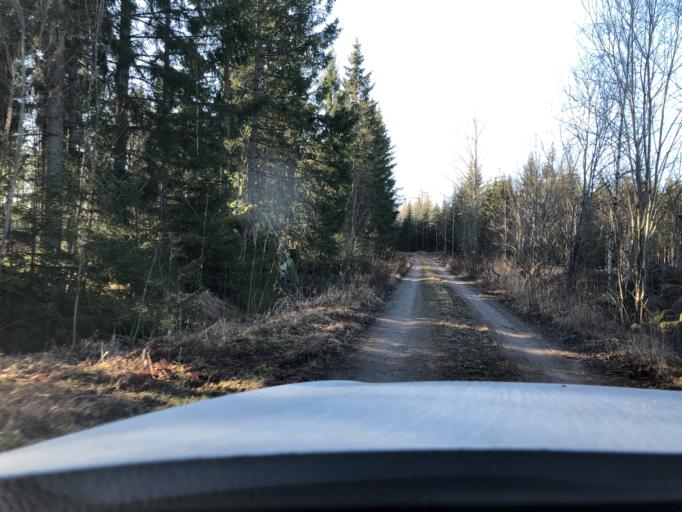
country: SE
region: Gaevleborg
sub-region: Gavle Kommun
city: Hedesunda
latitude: 60.3066
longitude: 16.8998
